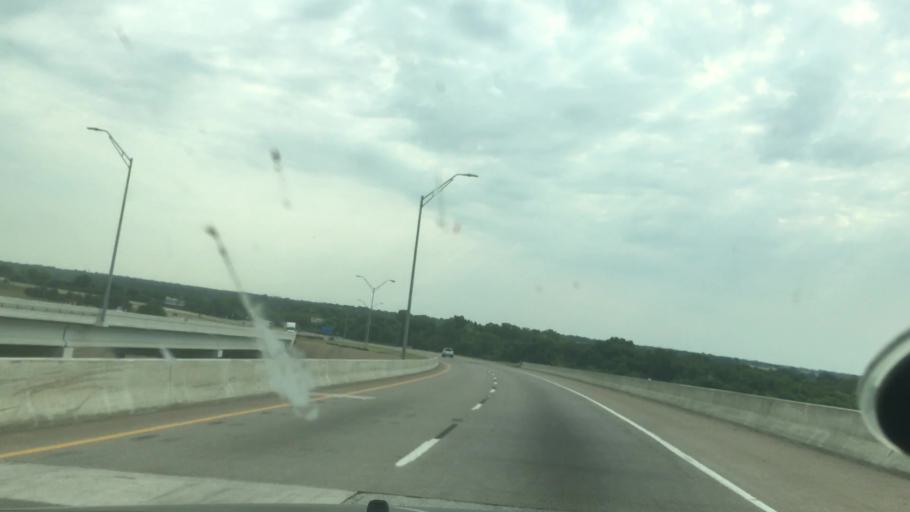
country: US
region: Texas
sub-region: Grayson County
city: Denison
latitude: 33.8012
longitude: -96.5383
